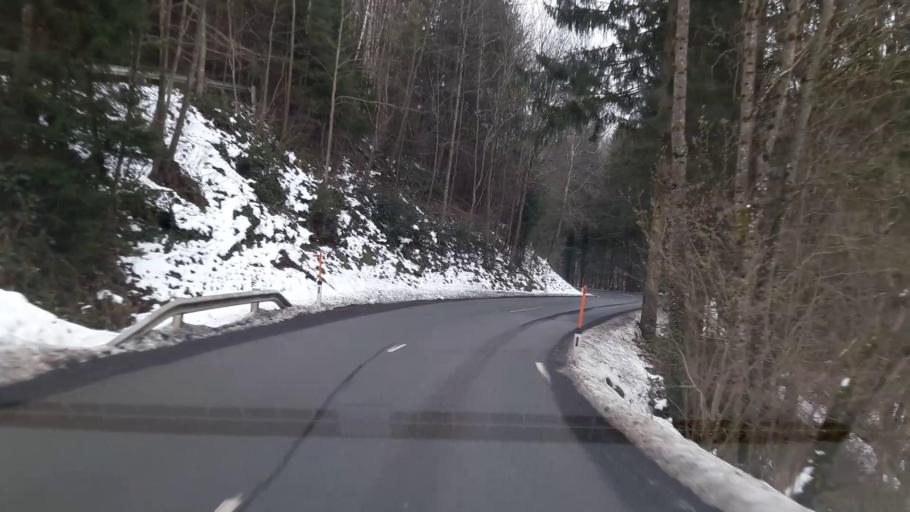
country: AT
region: Lower Austria
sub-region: Politischer Bezirk Neunkirchen
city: Feistritz am Wechsel
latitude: 47.5592
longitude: 16.0599
